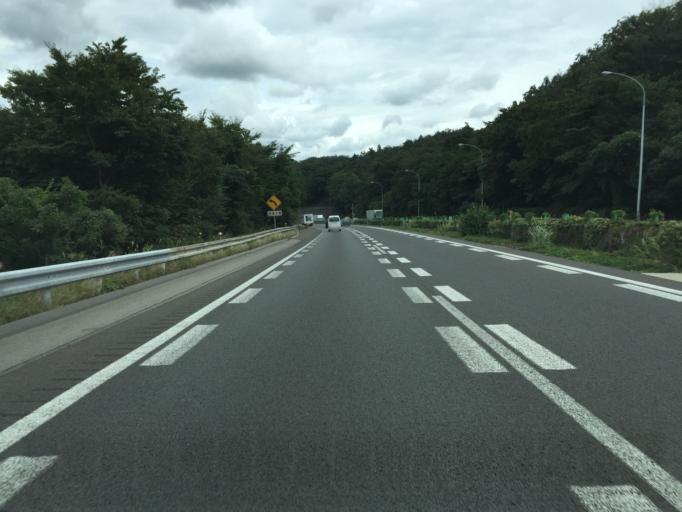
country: JP
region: Miyagi
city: Shiroishi
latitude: 37.9463
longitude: 140.6140
